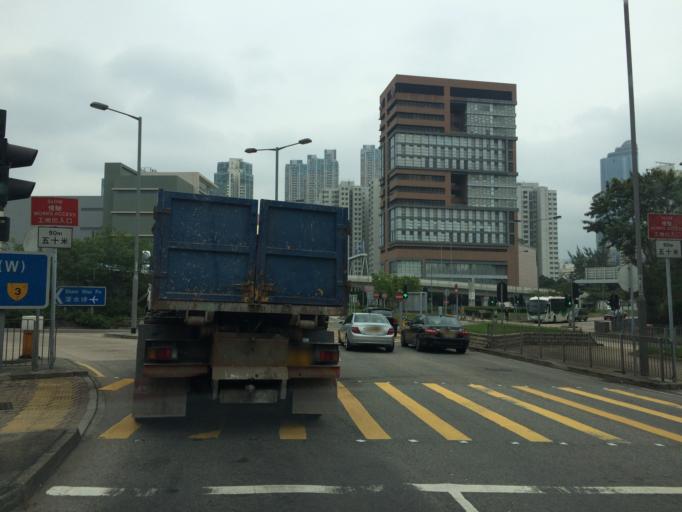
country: HK
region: Kowloon City
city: Kowloon
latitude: 22.3110
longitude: 114.1648
